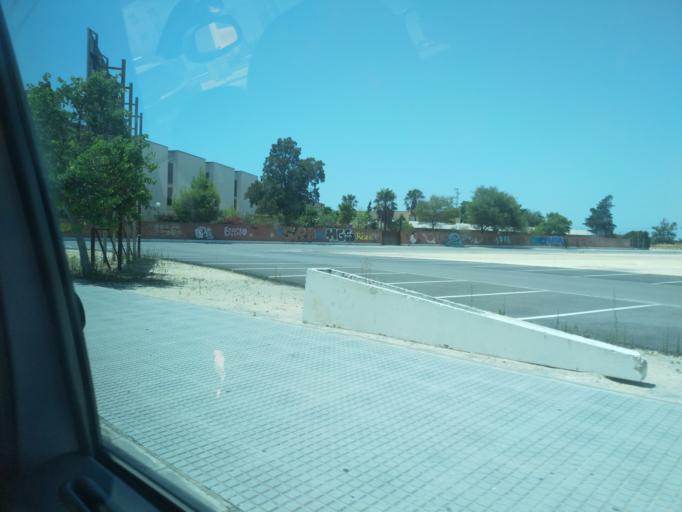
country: ES
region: Andalusia
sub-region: Provincia de Cadiz
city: Chiclana de la Frontera
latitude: 36.4211
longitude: -6.1562
